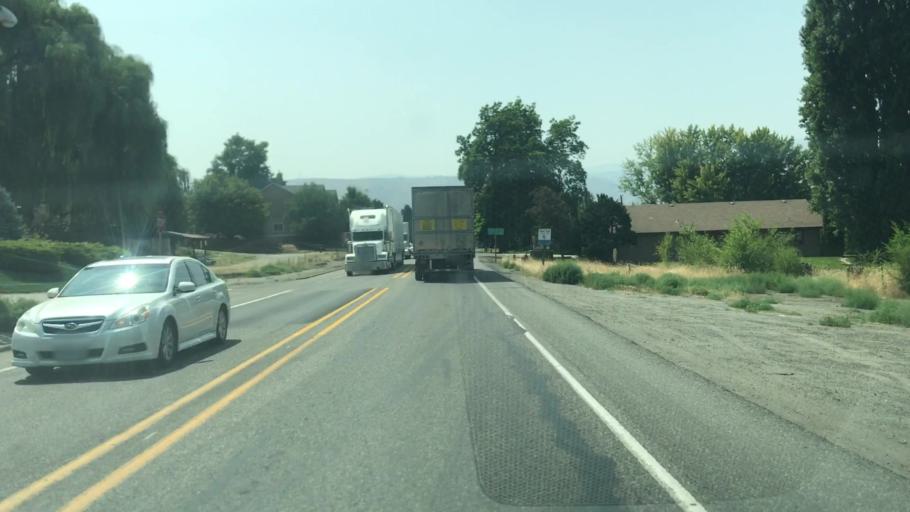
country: US
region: Washington
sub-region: Chelan County
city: Wenatchee
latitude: 47.4300
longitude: -120.2977
